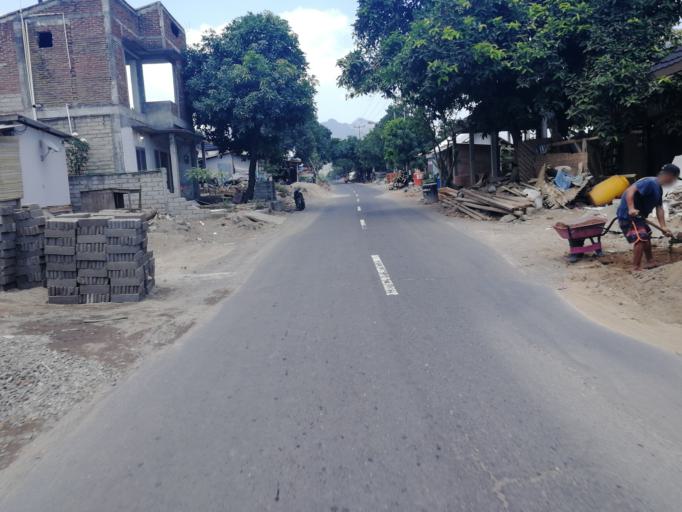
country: ID
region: West Nusa Tenggara
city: Karangsubagan
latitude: -8.4257
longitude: 116.0917
